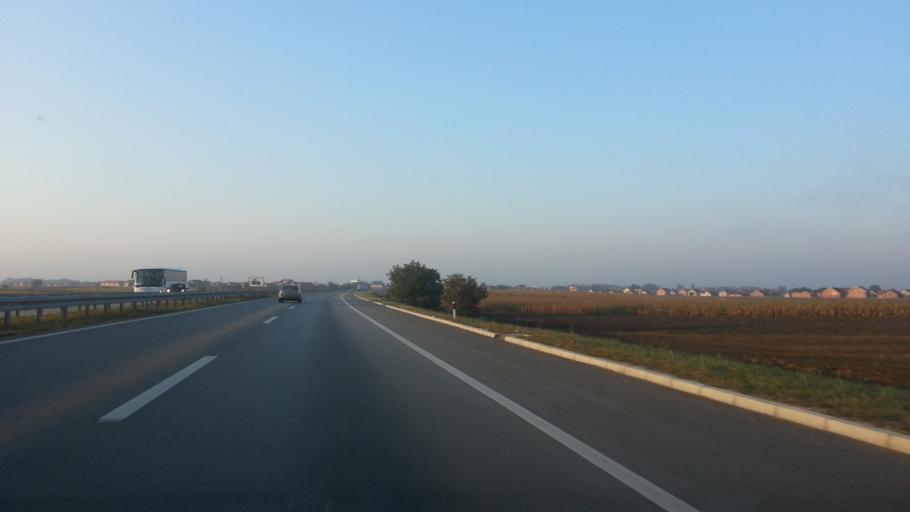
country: RS
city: Novi Banovci
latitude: 44.9072
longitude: 20.3047
